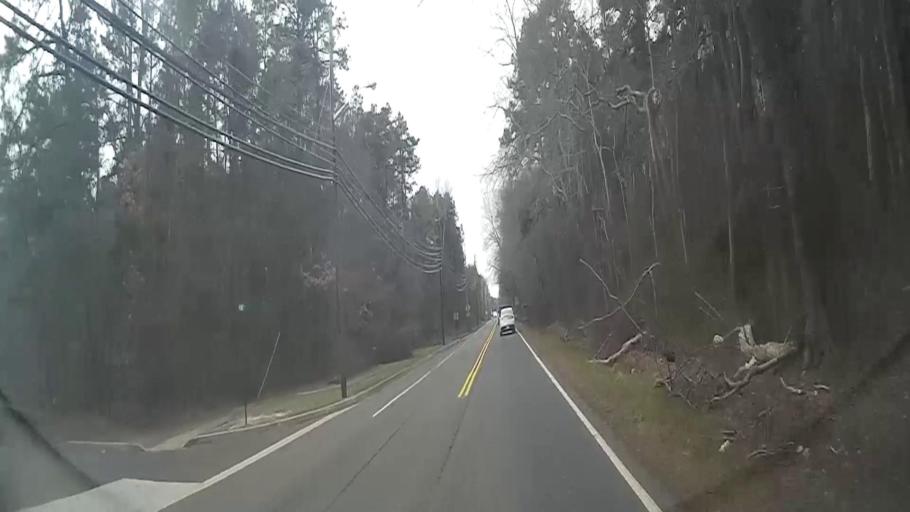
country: US
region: New Jersey
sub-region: Burlington County
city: Medford Lakes
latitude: 39.8556
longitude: -74.8622
